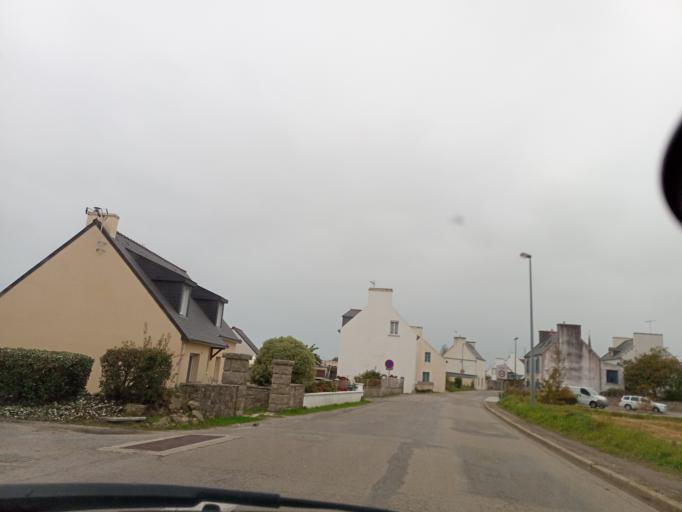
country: FR
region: Brittany
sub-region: Departement du Finistere
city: Esquibien
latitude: 48.0239
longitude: -4.5590
